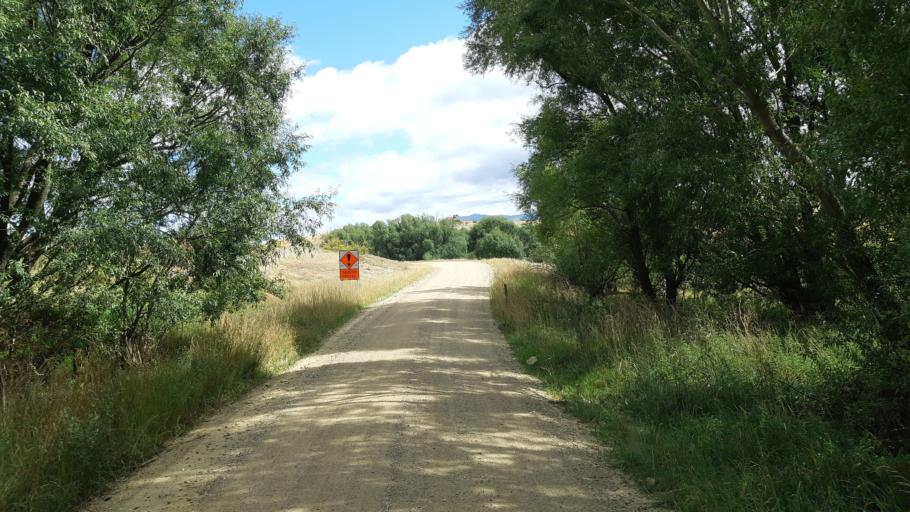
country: NZ
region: Otago
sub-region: Queenstown-Lakes District
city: Wanaka
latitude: -45.2107
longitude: 169.5525
